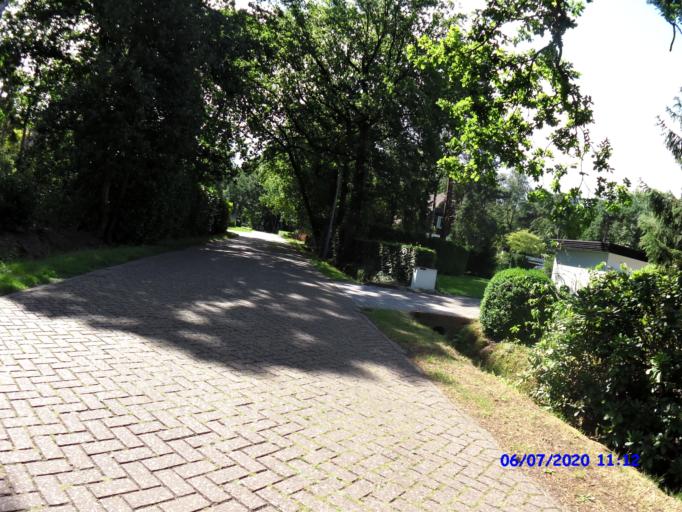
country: BE
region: Flanders
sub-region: Provincie Antwerpen
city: Oud-Turnhout
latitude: 51.3004
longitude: 5.0090
